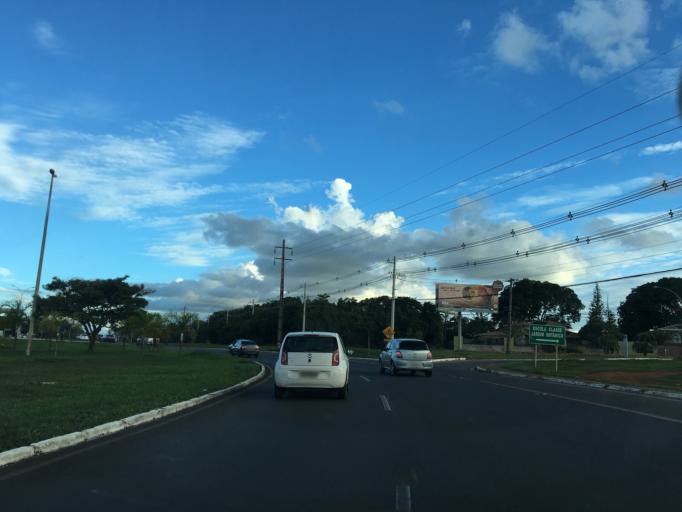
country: BR
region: Federal District
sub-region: Brasilia
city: Brasilia
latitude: -15.8580
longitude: -47.8339
